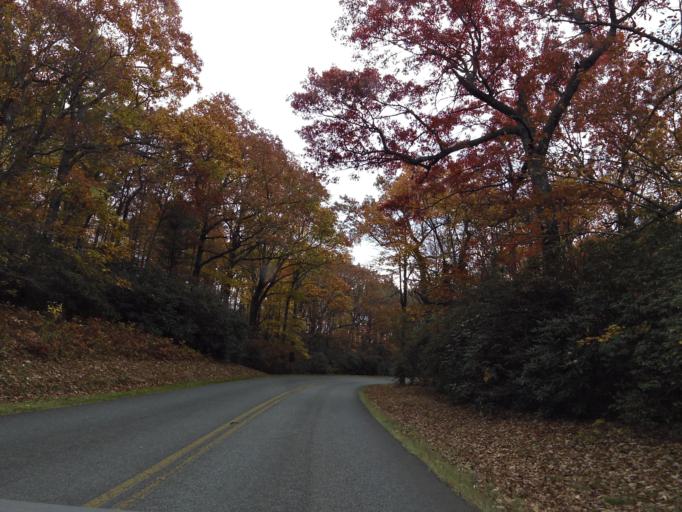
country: US
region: Virginia
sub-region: Carroll County
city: Cana
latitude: 36.6631
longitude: -80.6951
